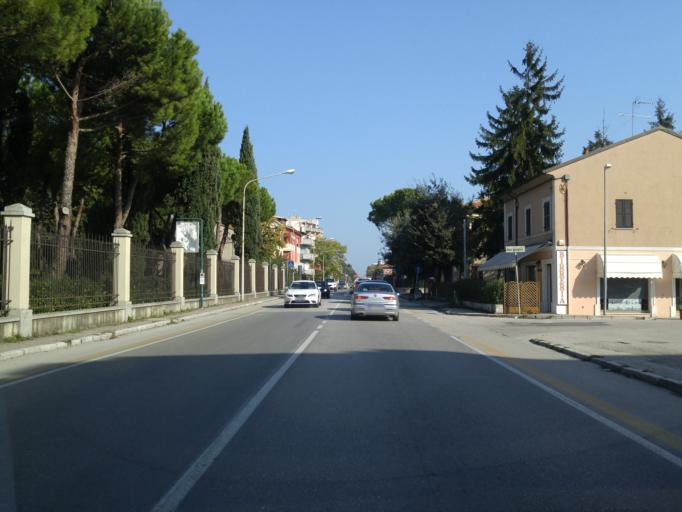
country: IT
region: The Marches
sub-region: Provincia di Pesaro e Urbino
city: Fano
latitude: 43.8378
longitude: 13.0081
